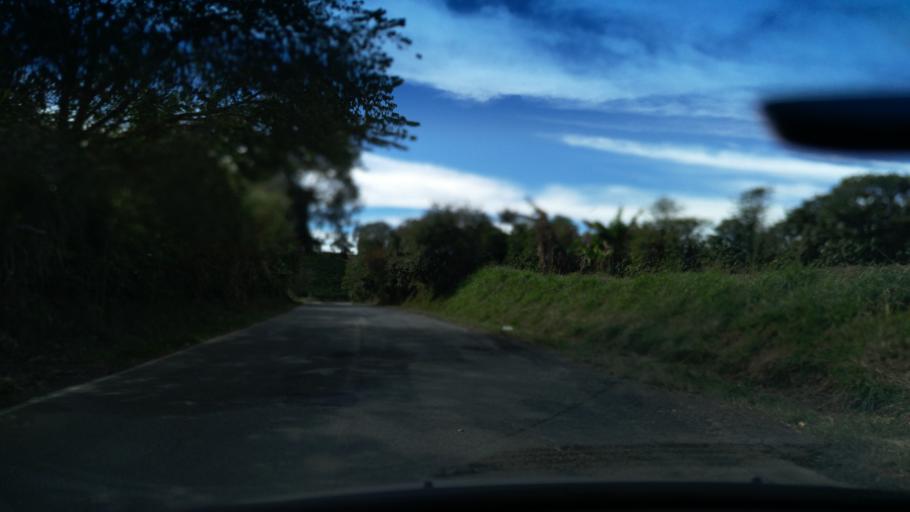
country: BR
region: Minas Gerais
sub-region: Andradas
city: Andradas
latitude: -22.0619
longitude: -46.3864
